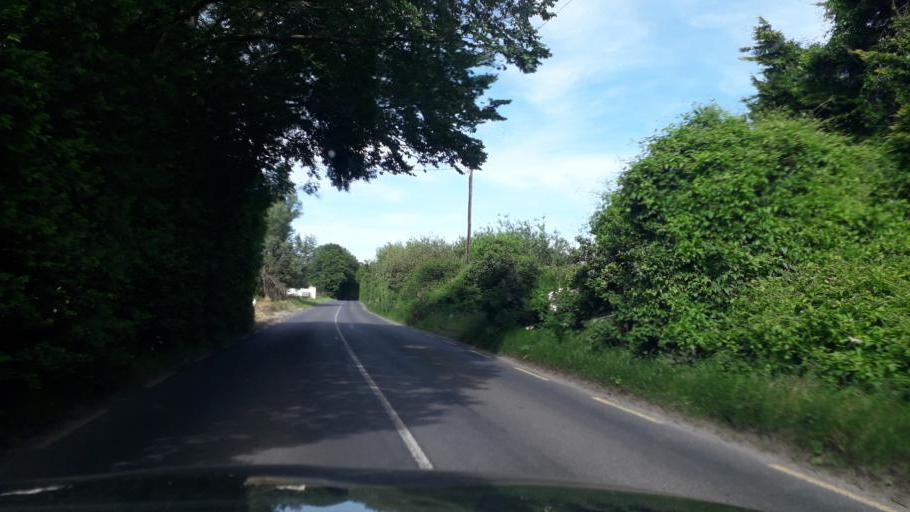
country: IE
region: Leinster
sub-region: Loch Garman
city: Castlebridge
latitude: 52.4020
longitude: -6.4323
